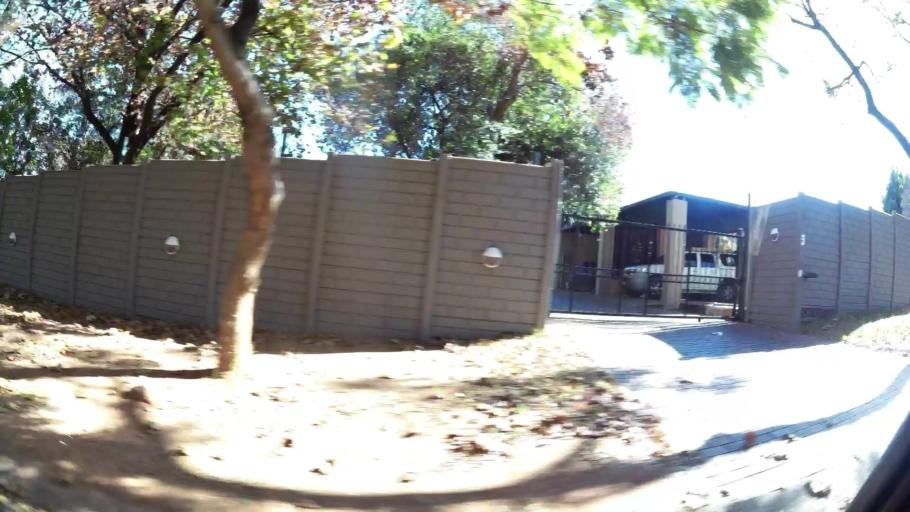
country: ZA
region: Gauteng
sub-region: City of Johannesburg Metropolitan Municipality
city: Roodepoort
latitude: -26.0982
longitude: 27.9538
